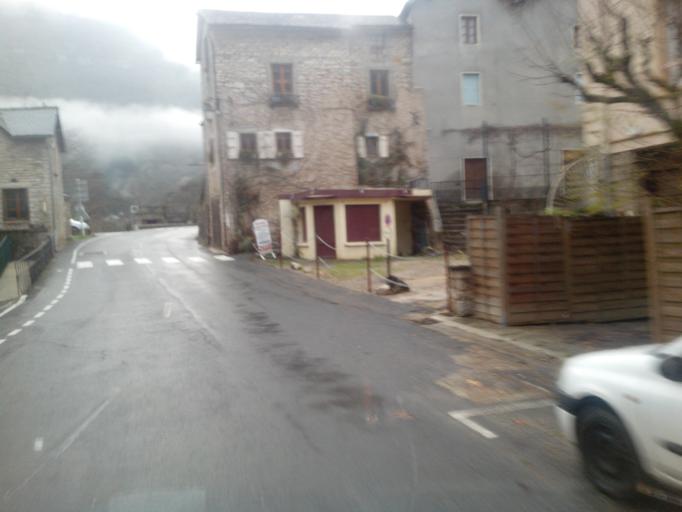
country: FR
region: Languedoc-Roussillon
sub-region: Departement de la Lozere
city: Meyrueis
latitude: 44.3014
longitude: 3.3200
